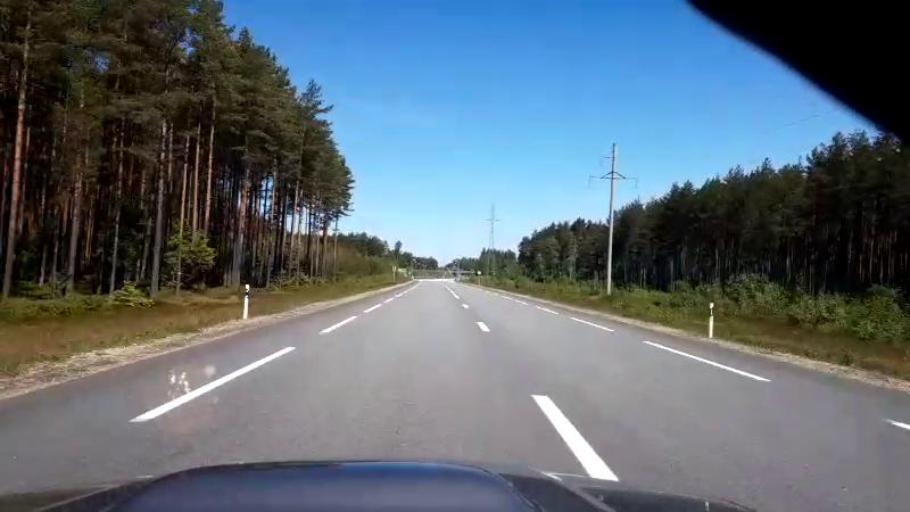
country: LV
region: Saulkrastu
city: Saulkrasti
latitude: 57.2411
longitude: 24.4270
